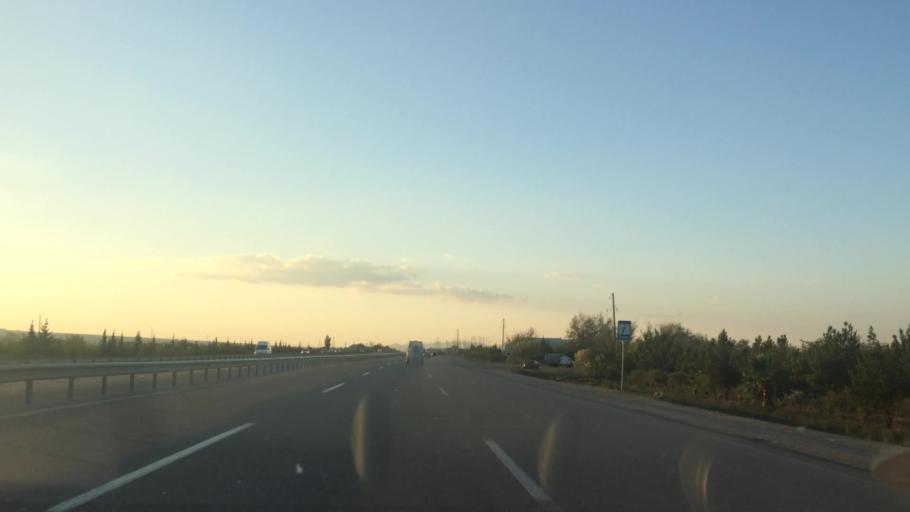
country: AZ
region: Haciqabul
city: Haciqabul
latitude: 40.0051
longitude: 49.1631
